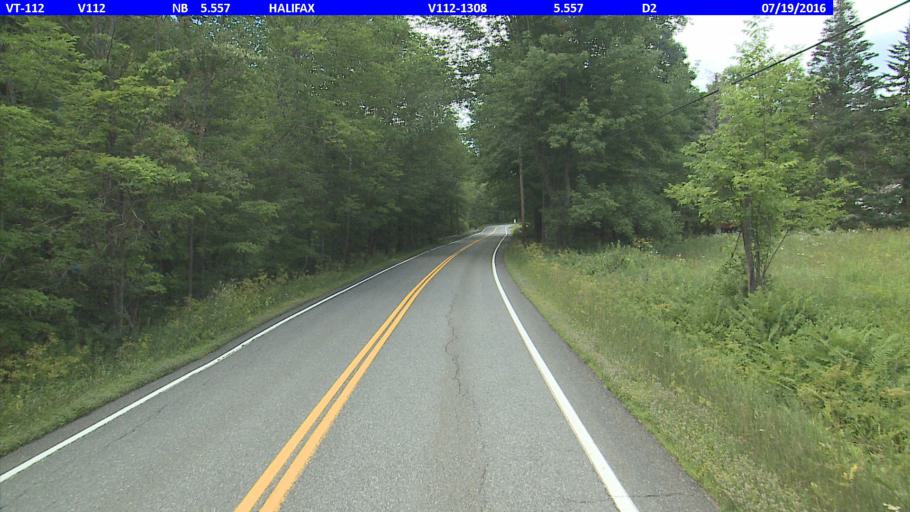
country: US
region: Massachusetts
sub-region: Franklin County
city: Colrain
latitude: 42.7751
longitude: -72.8033
